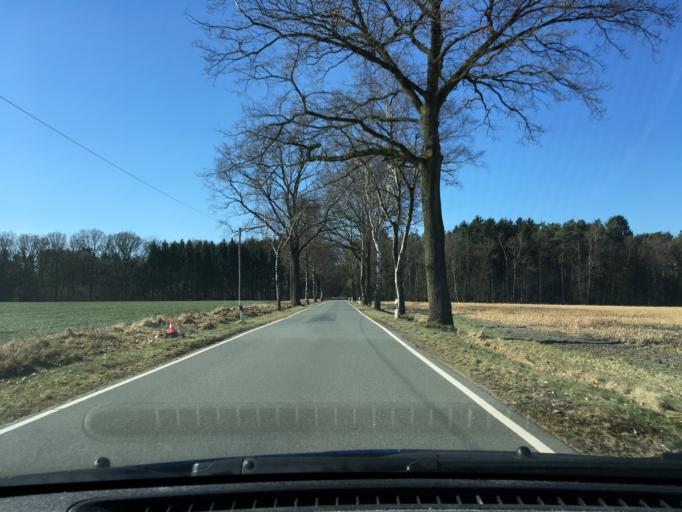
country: DE
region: Lower Saxony
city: Neuenkirchen
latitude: 53.0831
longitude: 9.7355
